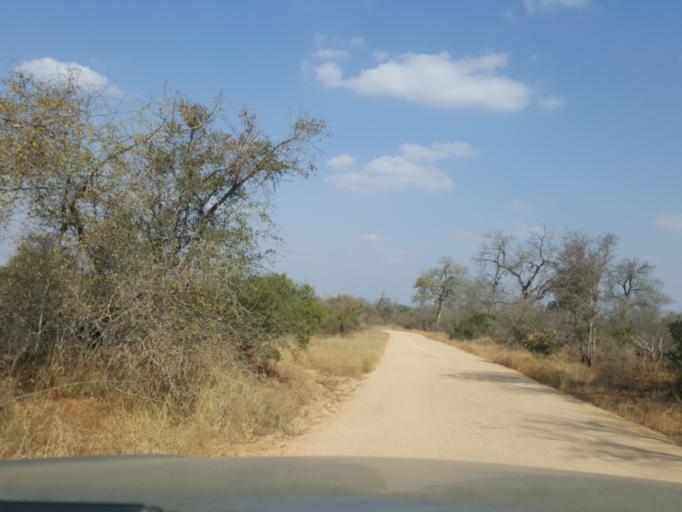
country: ZA
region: Mpumalanga
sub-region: Ehlanzeni District
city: Komatipoort
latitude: -25.2860
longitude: 31.7701
